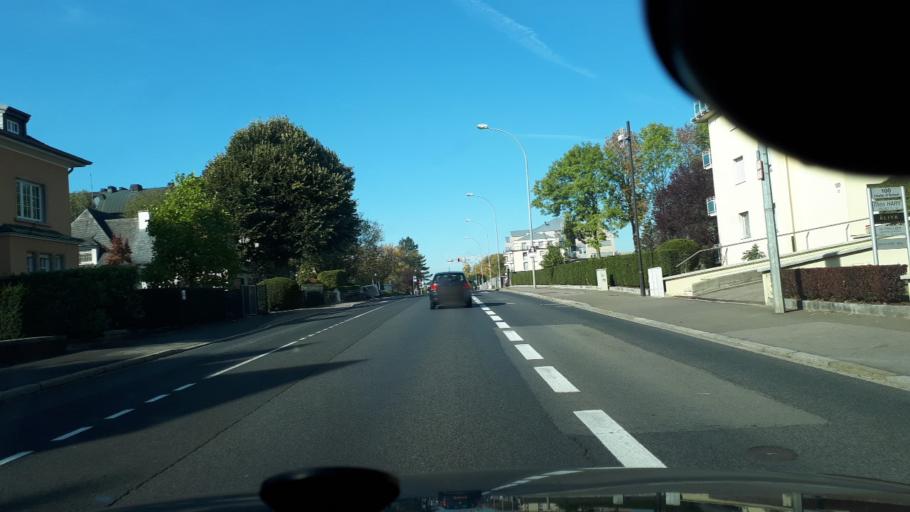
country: LU
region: Luxembourg
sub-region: Canton de Luxembourg
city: Luxembourg
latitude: 49.6156
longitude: 6.1049
